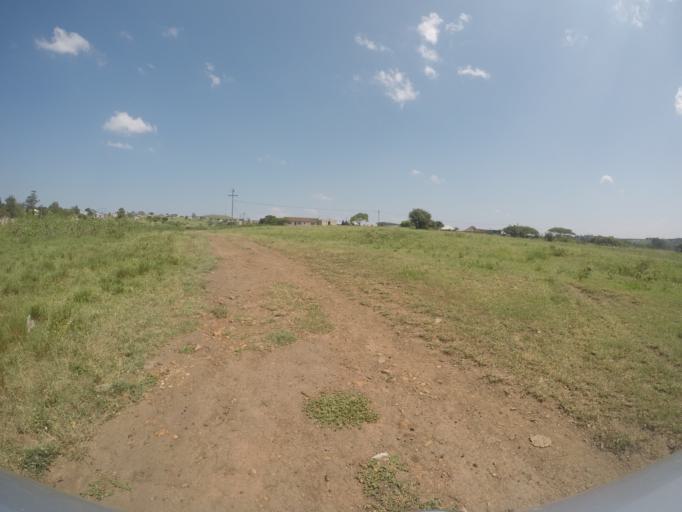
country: ZA
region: KwaZulu-Natal
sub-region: uThungulu District Municipality
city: Empangeni
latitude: -28.5874
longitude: 31.7404
